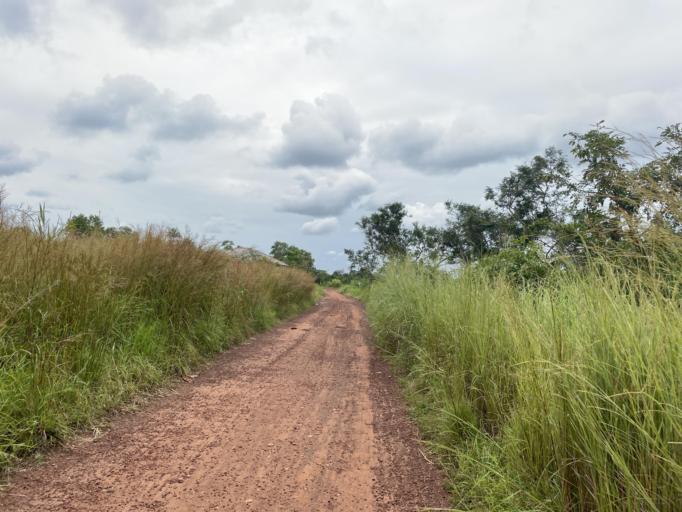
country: SL
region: Northern Province
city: Kambia
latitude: 9.1280
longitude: -12.9029
